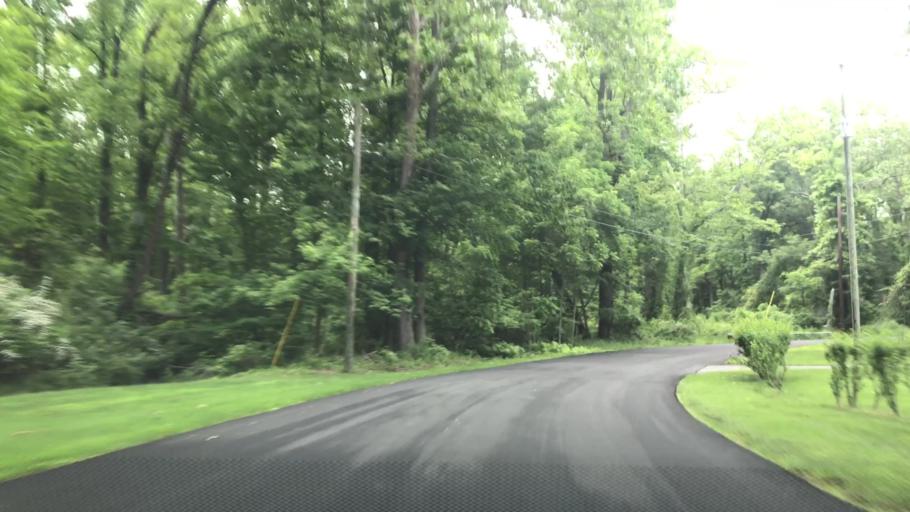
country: US
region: New Jersey
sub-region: Hunterdon County
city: Lebanon
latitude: 40.6615
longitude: -74.8339
